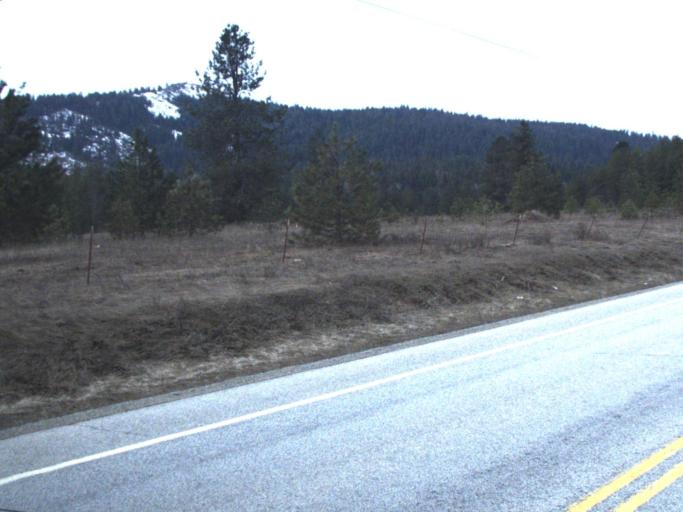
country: US
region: Washington
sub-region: Pend Oreille County
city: Newport
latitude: 48.2232
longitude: -117.1189
